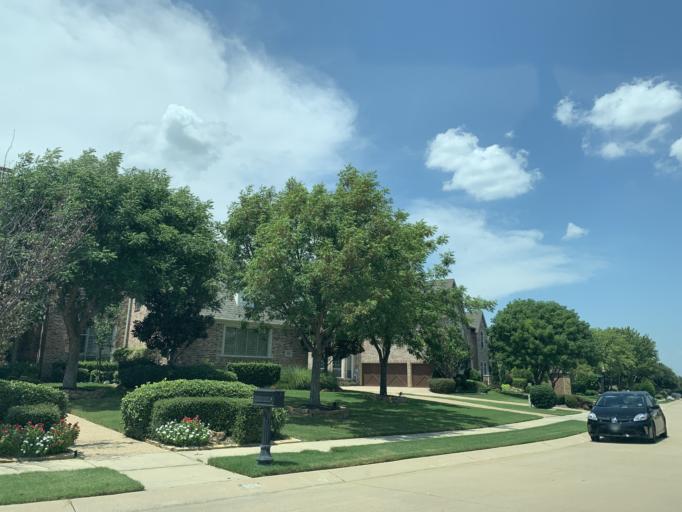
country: US
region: Texas
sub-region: Tarrant County
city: Southlake
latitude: 32.9715
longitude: -97.1517
